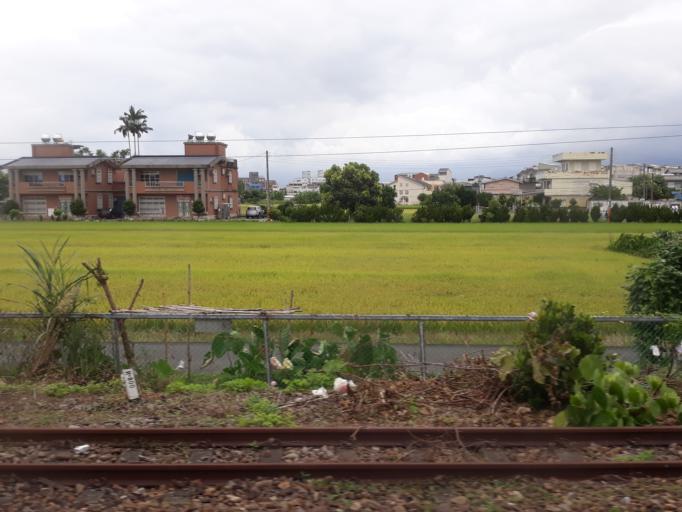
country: TW
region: Taiwan
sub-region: Yilan
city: Yilan
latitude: 24.7008
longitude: 121.7753
